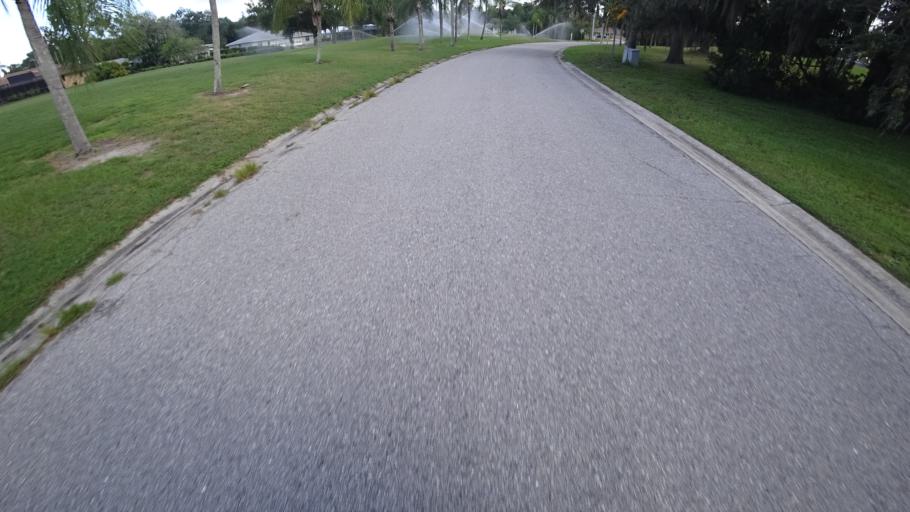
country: US
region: Florida
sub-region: Sarasota County
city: Desoto Lakes
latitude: 27.4051
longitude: -82.4996
